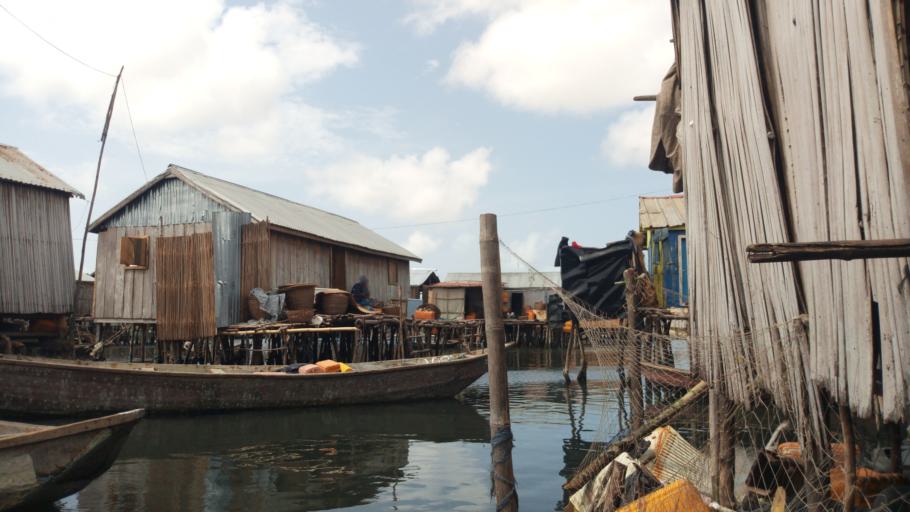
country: BJ
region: Littoral
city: Cotonou
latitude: 6.3910
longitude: 2.4334
